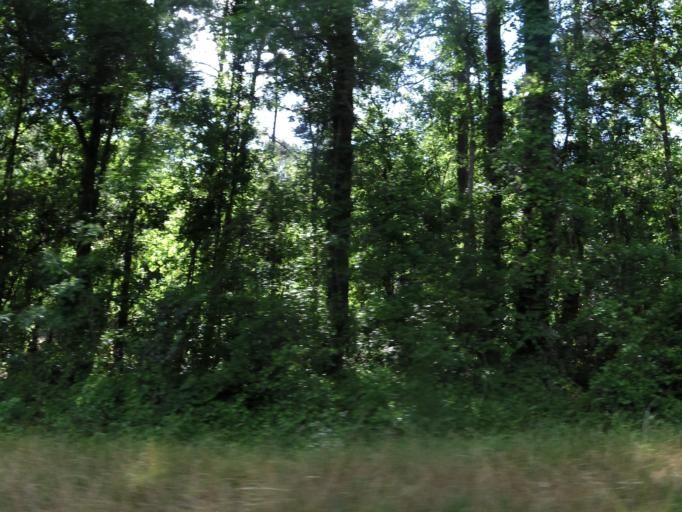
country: US
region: South Carolina
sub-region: Allendale County
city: Fairfax
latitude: 32.9438
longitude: -81.2368
